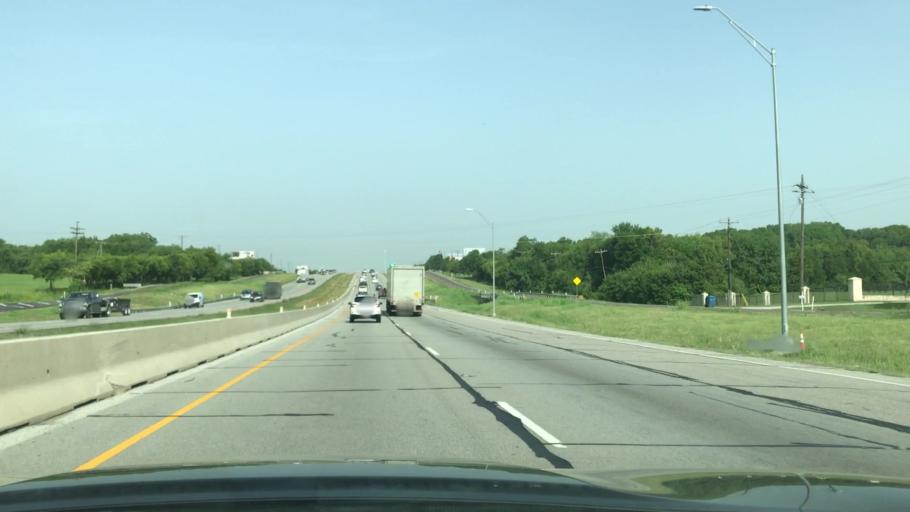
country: US
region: Texas
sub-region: Dallas County
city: Sunnyvale
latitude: 32.7817
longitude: -96.5423
